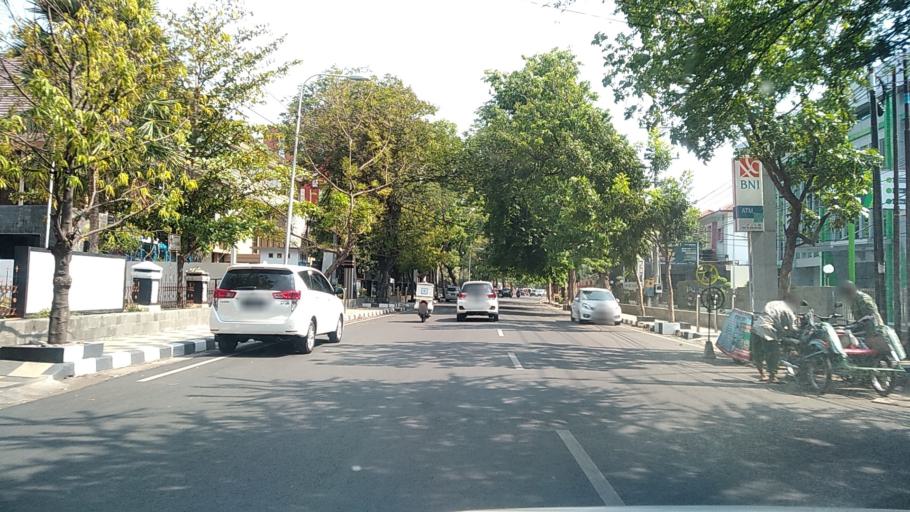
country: ID
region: Central Java
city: Semarang
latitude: -6.9874
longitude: 110.4294
